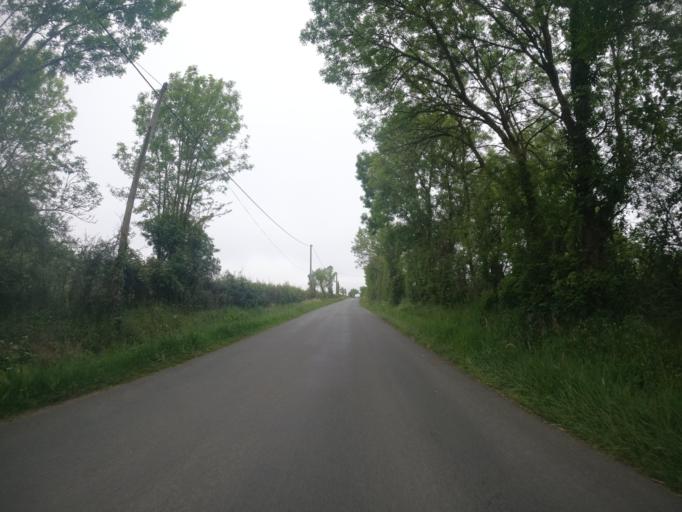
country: FR
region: Poitou-Charentes
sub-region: Departement des Deux-Sevres
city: Saint-Varent
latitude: 46.8725
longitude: -0.3107
